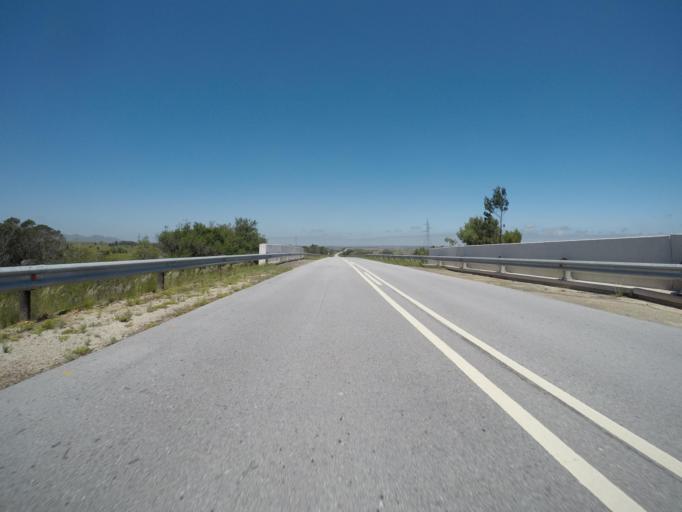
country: ZA
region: Eastern Cape
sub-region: Cacadu District Municipality
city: Kruisfontein
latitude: -33.9983
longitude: 24.5422
